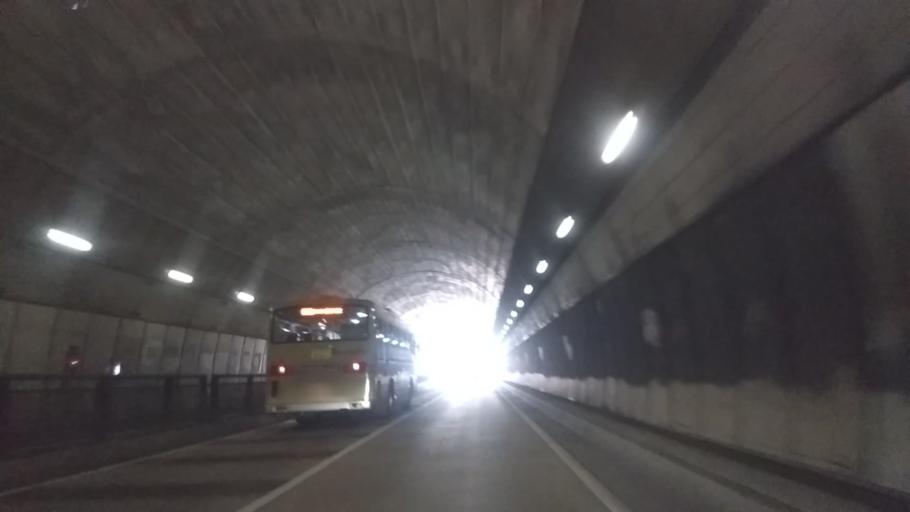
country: JP
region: Kanagawa
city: Fujisawa
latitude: 35.3498
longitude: 139.4461
